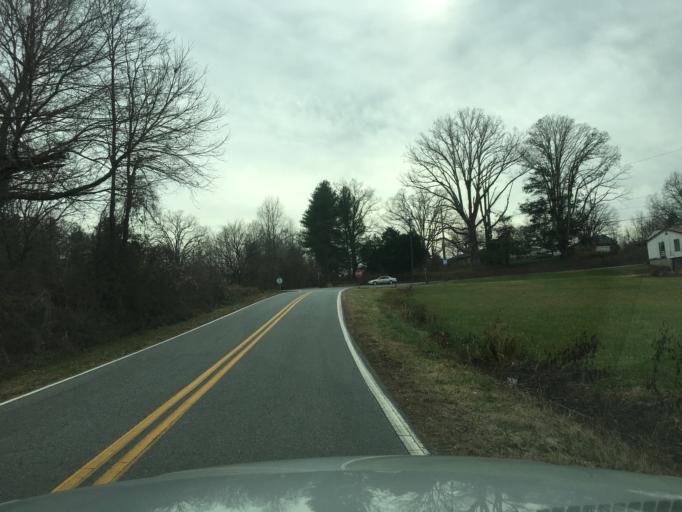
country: US
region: North Carolina
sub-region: McDowell County
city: West Marion
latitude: 35.6158
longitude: -81.9746
